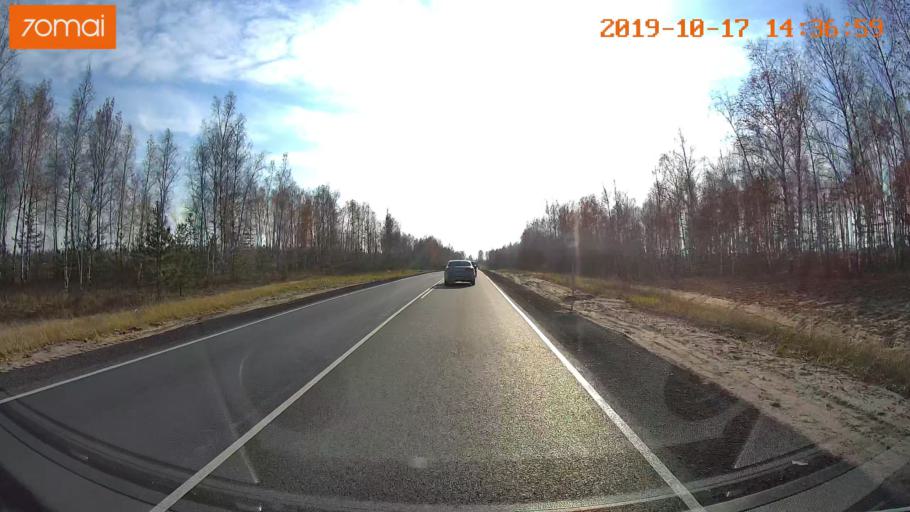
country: RU
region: Rjazan
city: Solotcha
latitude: 54.8842
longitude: 40.0001
